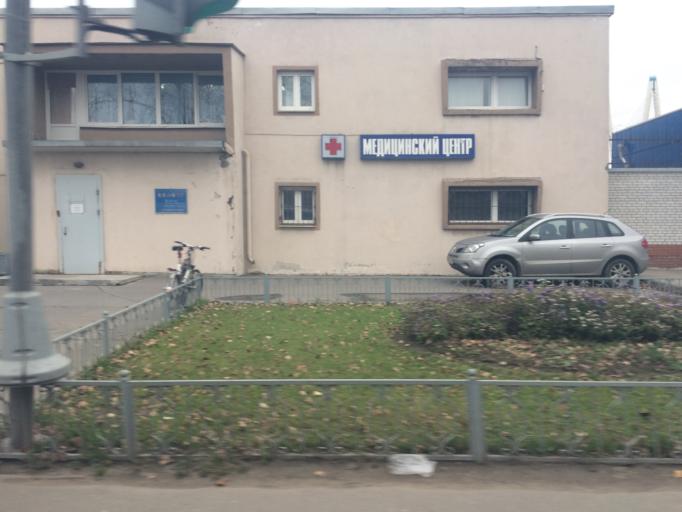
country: RU
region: Leningrad
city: Rybatskoye
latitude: 59.8549
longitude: 30.4807
